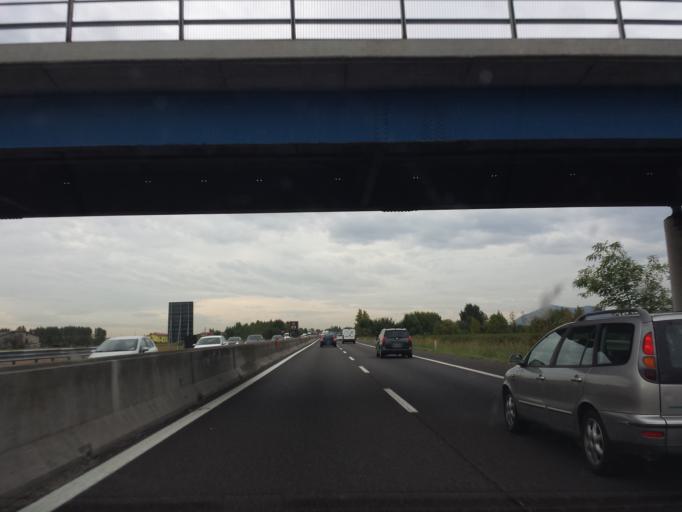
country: IT
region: Veneto
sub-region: Provincia di Padova
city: Terradura
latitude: 45.3112
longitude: 11.8232
